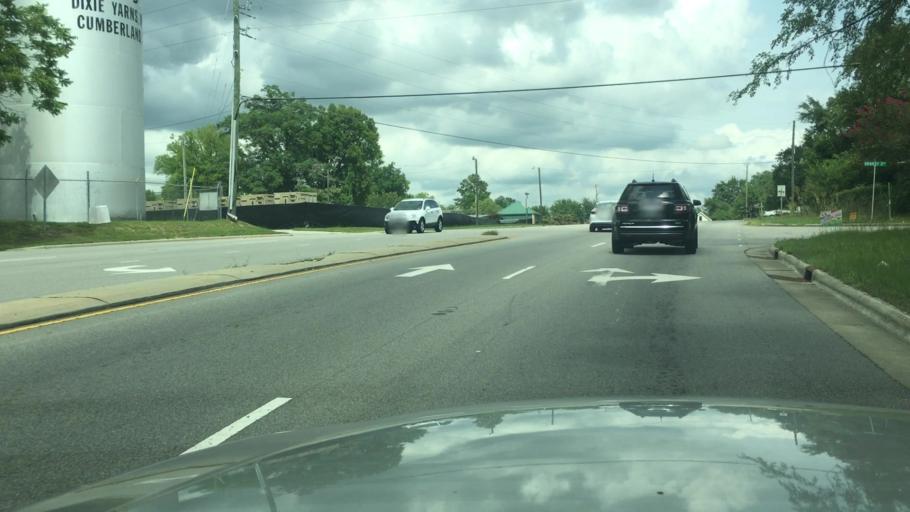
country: US
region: North Carolina
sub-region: Cumberland County
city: Hope Mills
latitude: 35.0019
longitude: -78.9751
